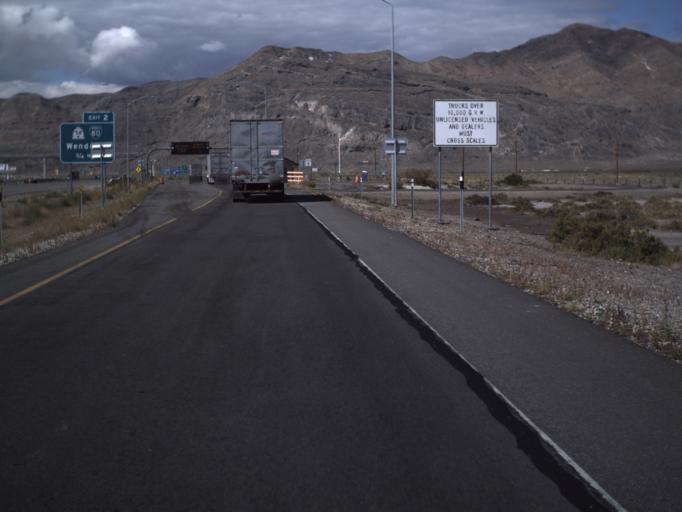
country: US
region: Utah
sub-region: Tooele County
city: Wendover
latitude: 40.7448
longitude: -113.9869
